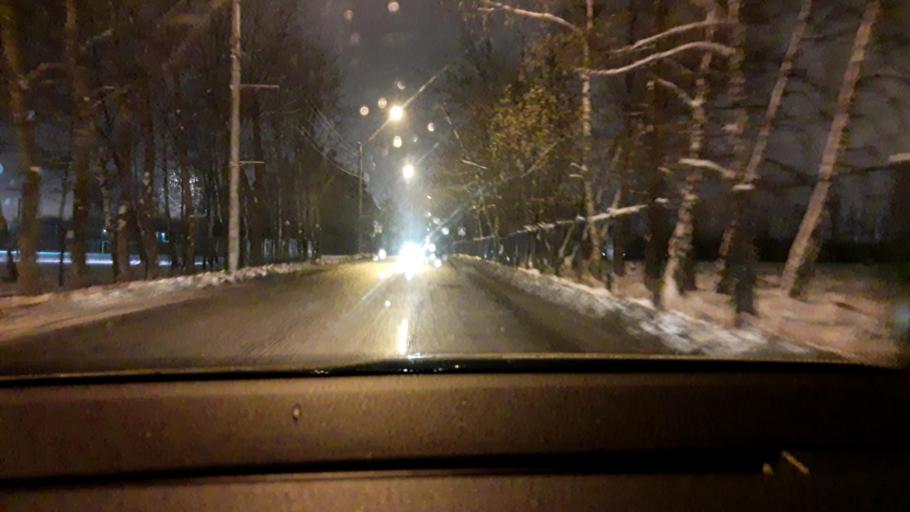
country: RU
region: Moskovskaya
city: Biryulevo Zapadnoye
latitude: 55.5660
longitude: 37.6407
